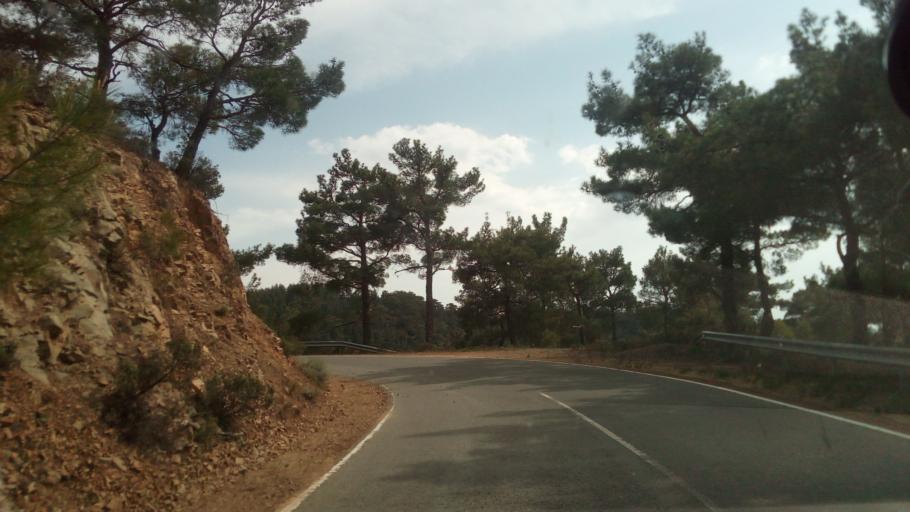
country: CY
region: Lefkosia
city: Kato Pyrgos
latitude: 35.0250
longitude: 32.6579
